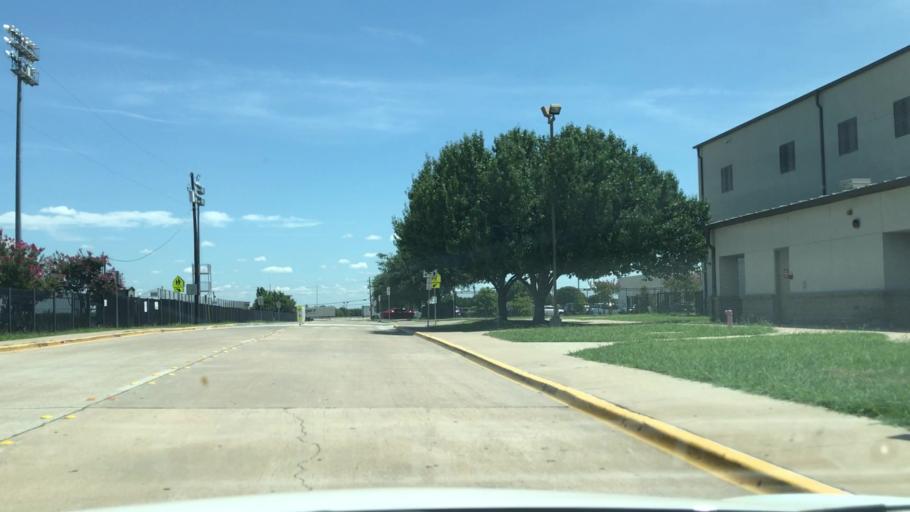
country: US
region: Texas
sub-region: Rockwall County
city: Rockwall
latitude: 32.9061
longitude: -96.4563
